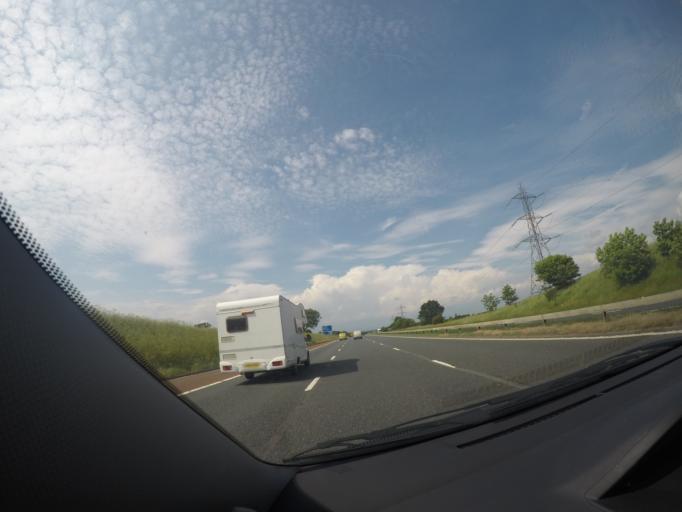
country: GB
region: England
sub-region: Cumbria
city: Scotby
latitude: 54.8829
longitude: -2.8829
